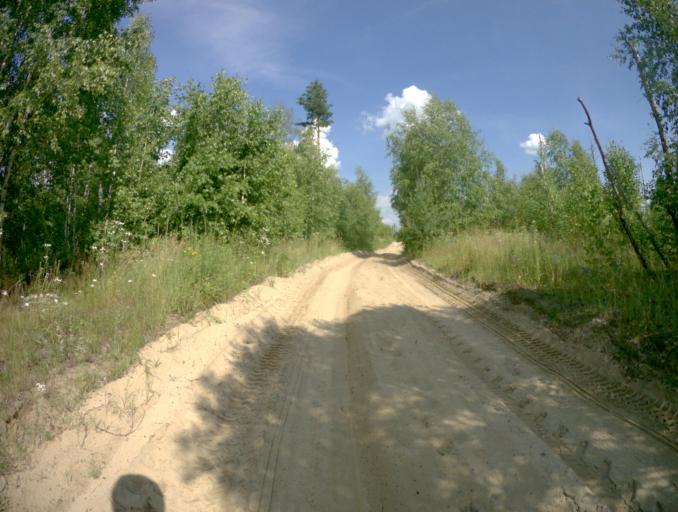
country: RU
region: Ivanovo
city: Talitsy
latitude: 56.5388
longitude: 42.2678
